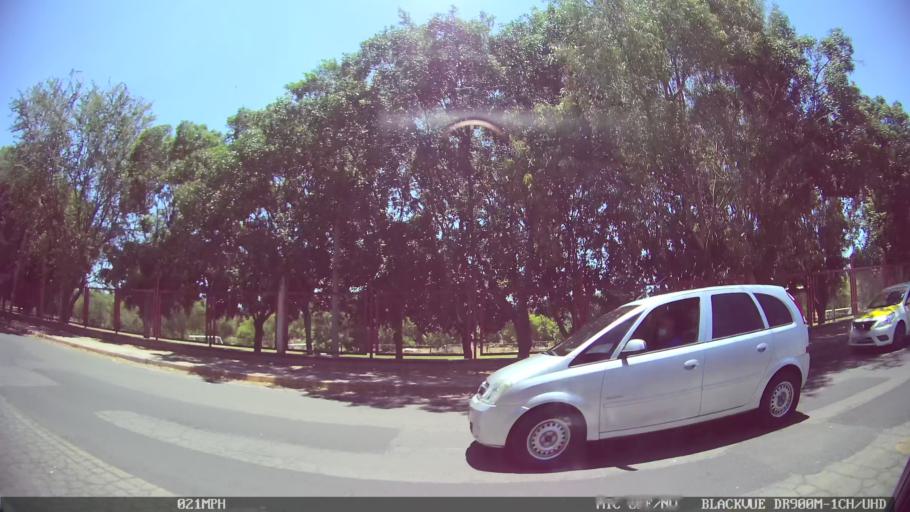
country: MX
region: Jalisco
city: Tlaquepaque
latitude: 20.6641
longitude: -103.2703
